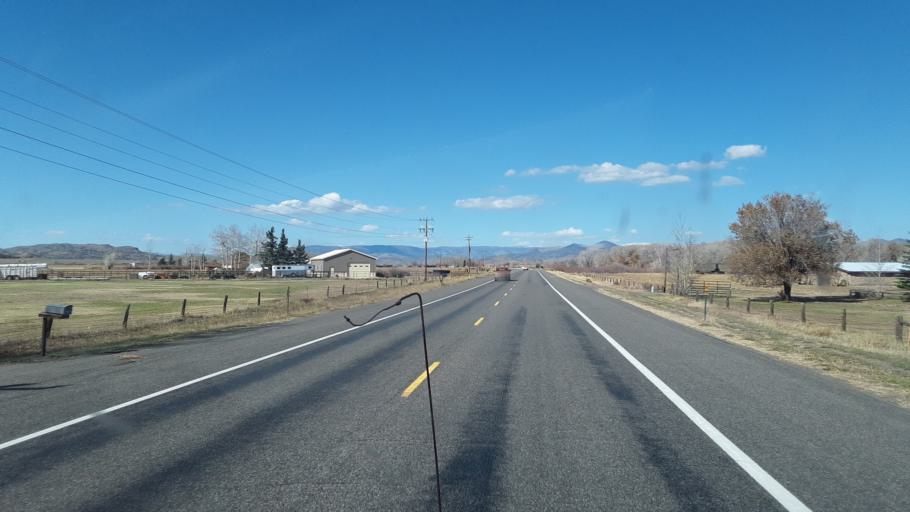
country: US
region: Colorado
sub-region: Rio Grande County
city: Del Norte
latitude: 37.6548
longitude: -106.2847
